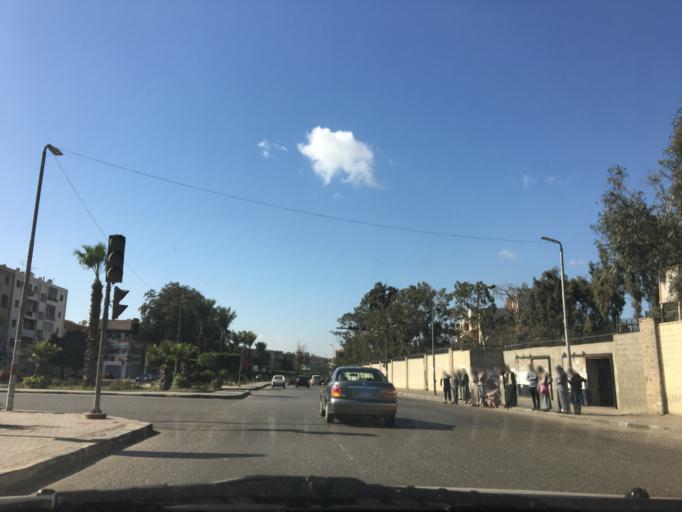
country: EG
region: Muhafazat al Qahirah
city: Cairo
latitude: 30.0511
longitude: 31.3208
